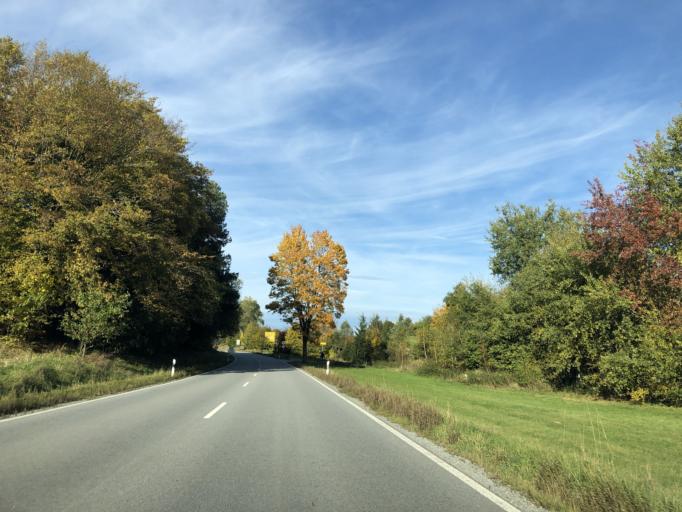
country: DE
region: Bavaria
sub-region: Lower Bavaria
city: Ruhmannsfelden
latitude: 48.9740
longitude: 12.9792
